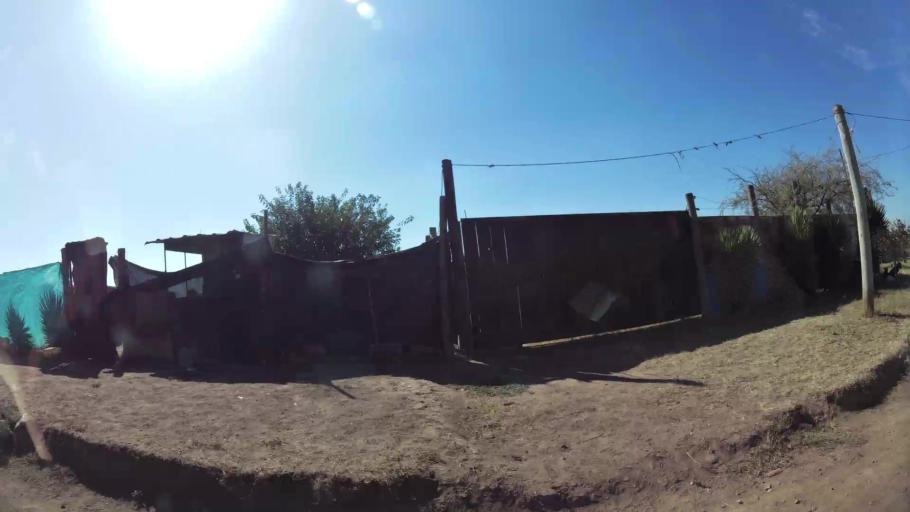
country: AR
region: Cordoba
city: Villa Allende
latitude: -31.3261
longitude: -64.2447
